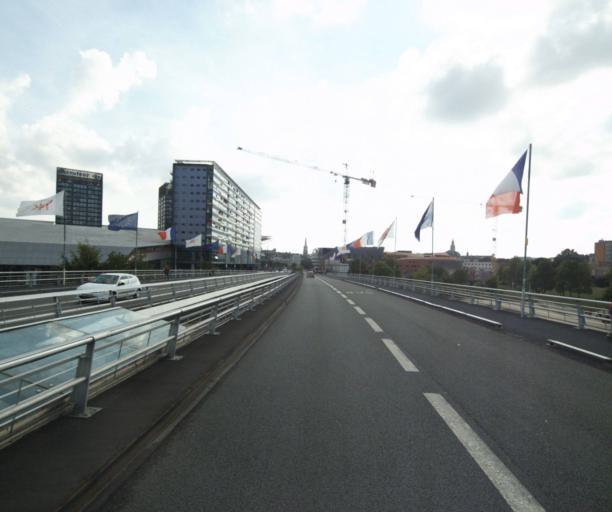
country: FR
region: Nord-Pas-de-Calais
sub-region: Departement du Nord
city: La Madeleine
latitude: 50.6393
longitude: 3.0749
